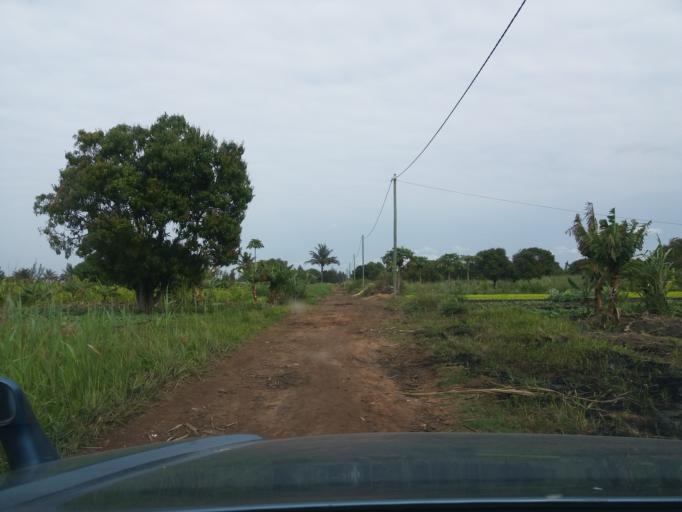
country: MZ
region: Maputo City
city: Maputo
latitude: -25.8933
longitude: 32.6361
